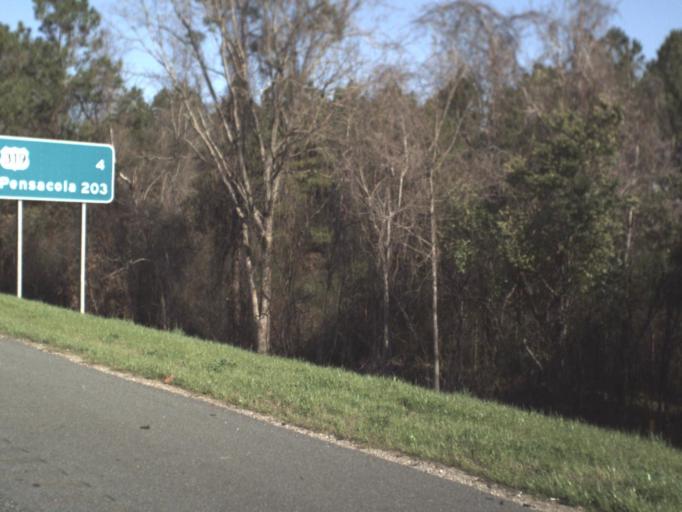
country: US
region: Florida
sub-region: Leon County
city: Tallahassee
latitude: 30.4961
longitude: -84.1747
